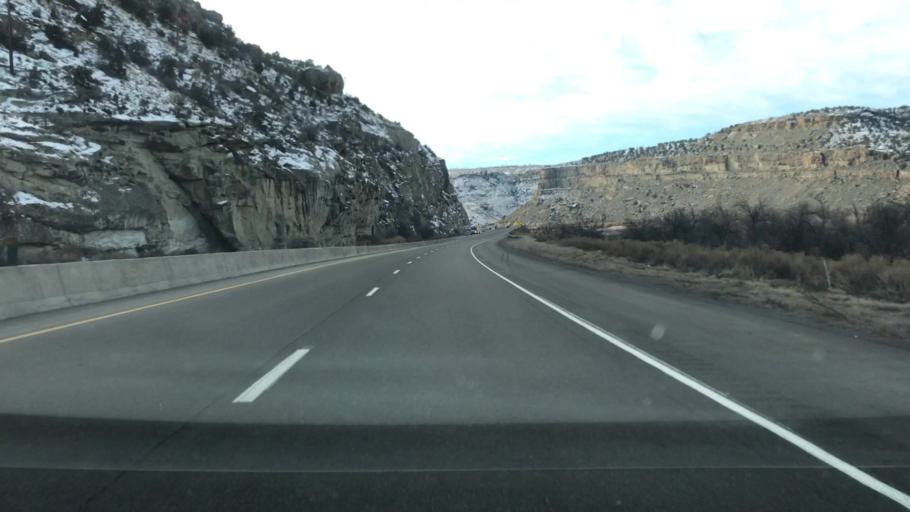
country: US
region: Colorado
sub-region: Mesa County
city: Palisade
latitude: 39.2666
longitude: -108.2547
